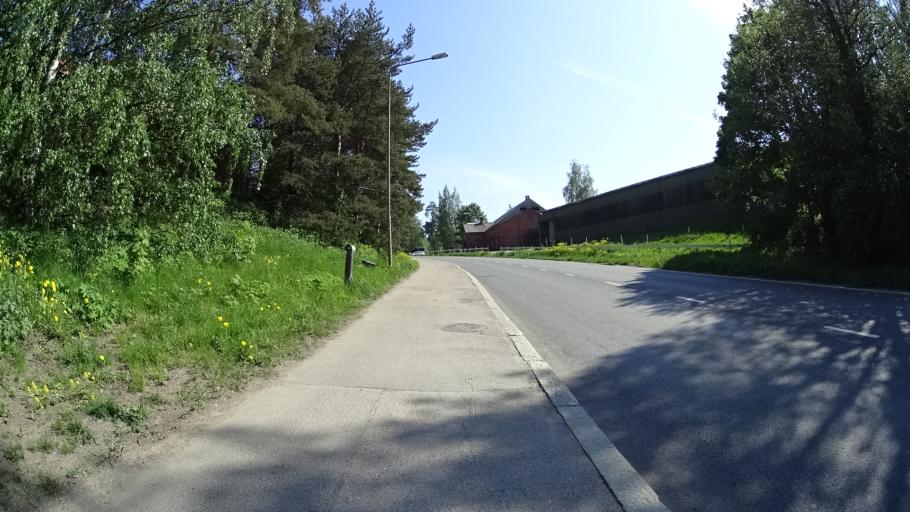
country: FI
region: Uusimaa
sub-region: Helsinki
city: Otaniemi
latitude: 60.1830
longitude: 24.8167
